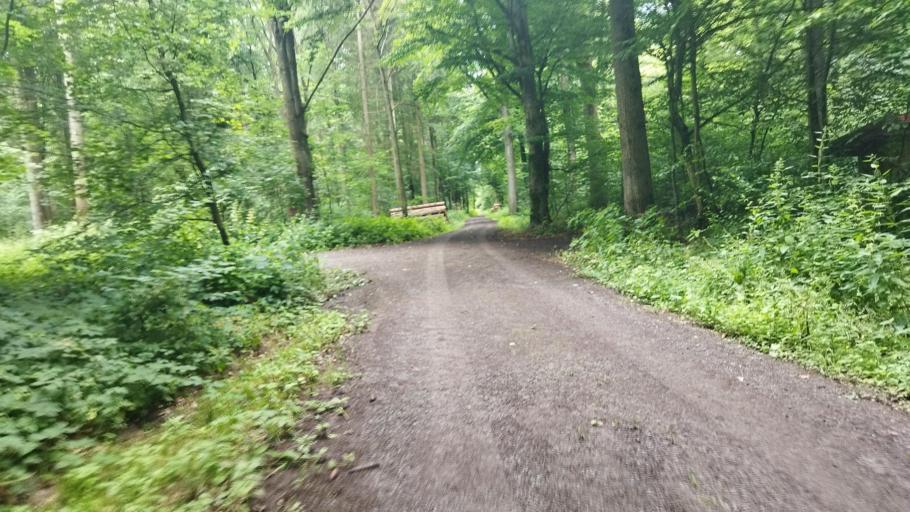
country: DE
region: Baden-Wuerttemberg
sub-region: Regierungsbezirk Stuttgart
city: Bad Rappenau
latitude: 49.2054
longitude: 9.1150
